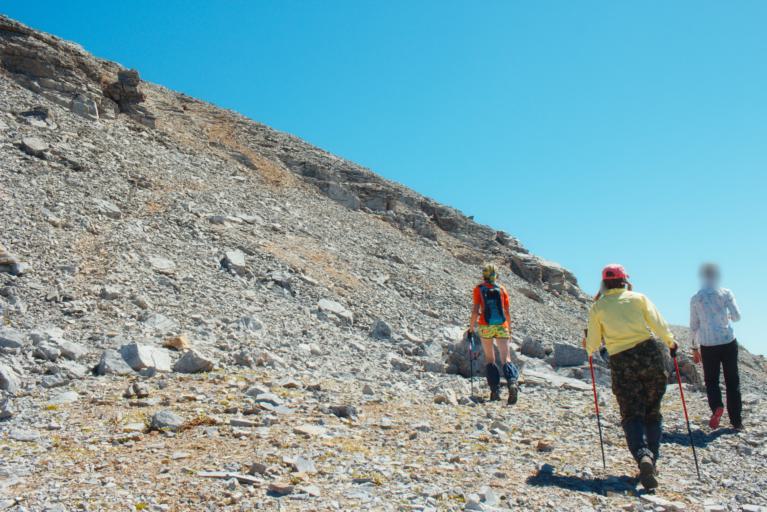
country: RU
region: Karachayevo-Cherkesiya
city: Nizhniy Arkhyz
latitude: 43.5836
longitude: 41.1982
